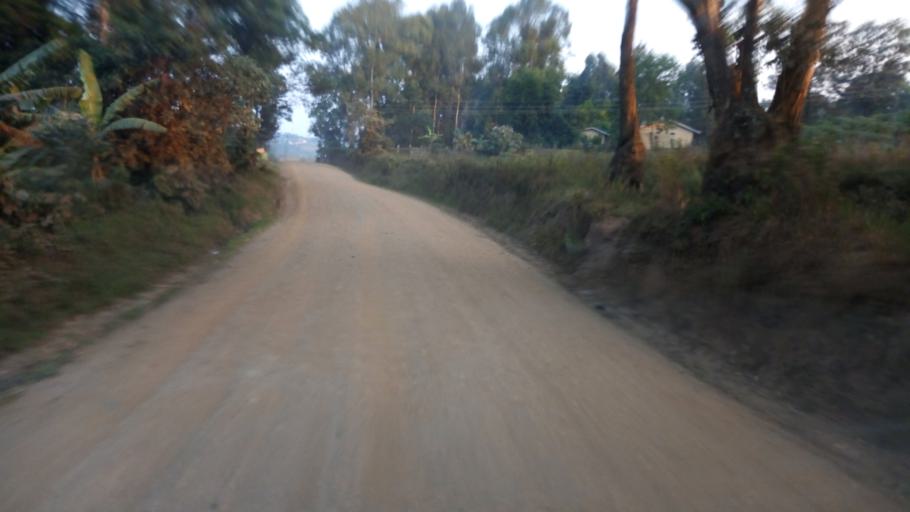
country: UG
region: Western Region
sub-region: Rukungiri District
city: Rukungiri
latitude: -0.7718
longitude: 29.9263
